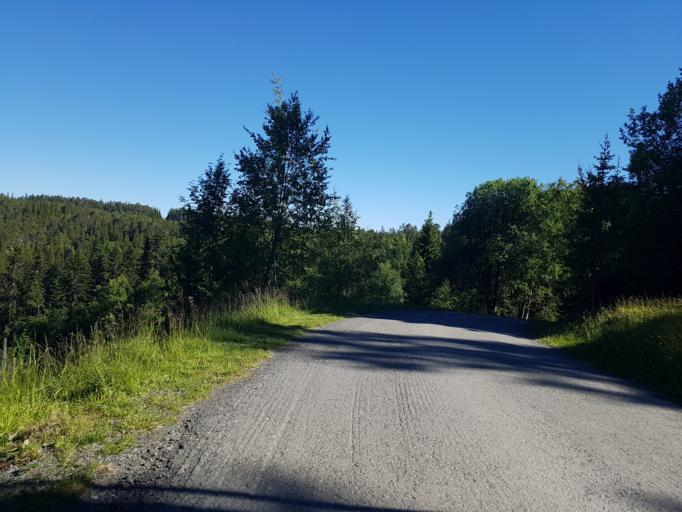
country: NO
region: Sor-Trondelag
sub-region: Trondheim
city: Trondheim
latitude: 63.4328
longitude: 10.2761
